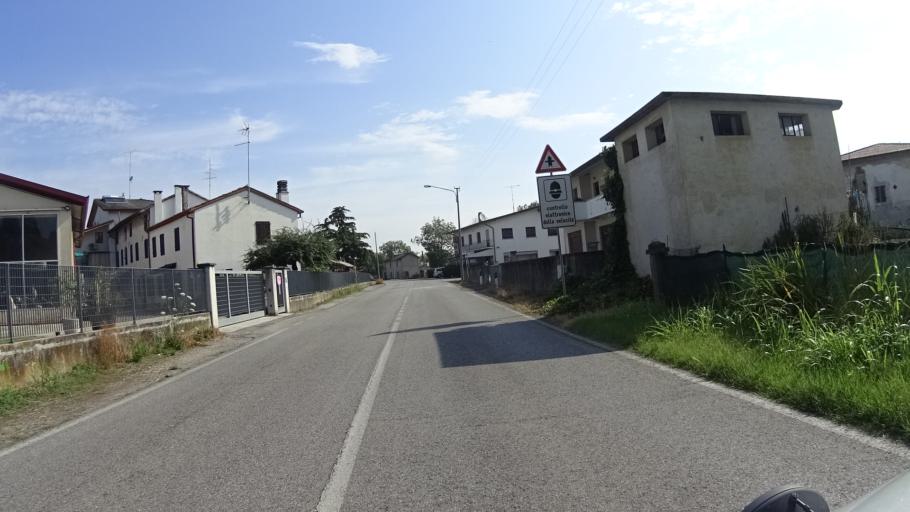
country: IT
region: Veneto
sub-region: Provincia di Venezia
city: Lugugnana
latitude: 45.7274
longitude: 12.9567
